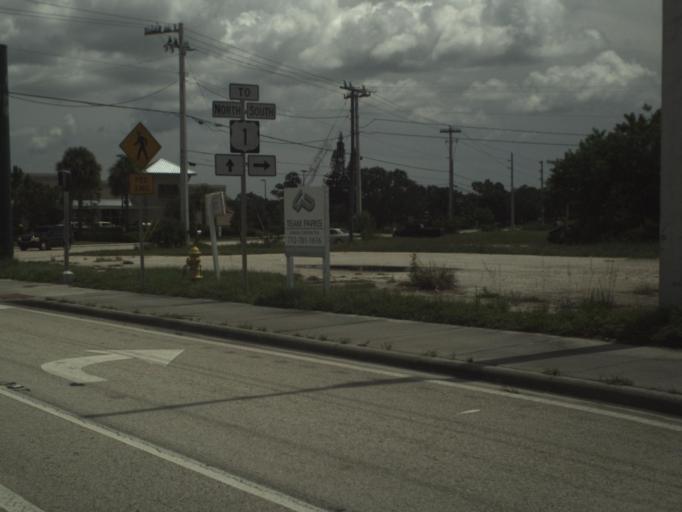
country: US
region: Florida
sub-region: Martin County
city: Palm City
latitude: 27.1236
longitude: -80.2523
